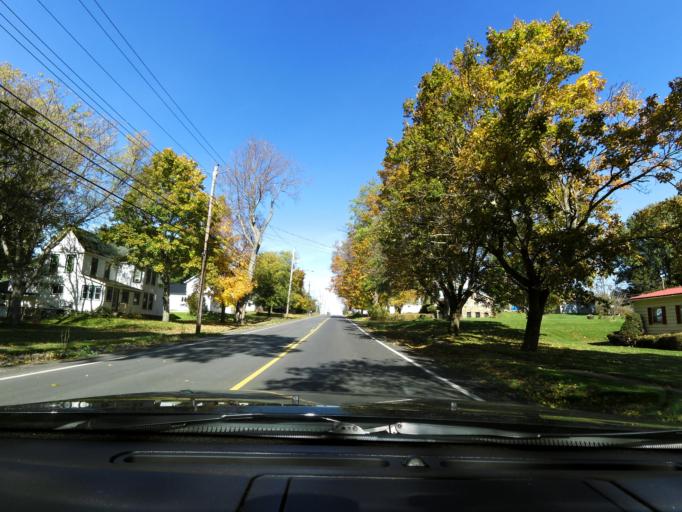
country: US
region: New York
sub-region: Wyoming County
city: Castile
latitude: 42.6442
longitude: -78.1341
